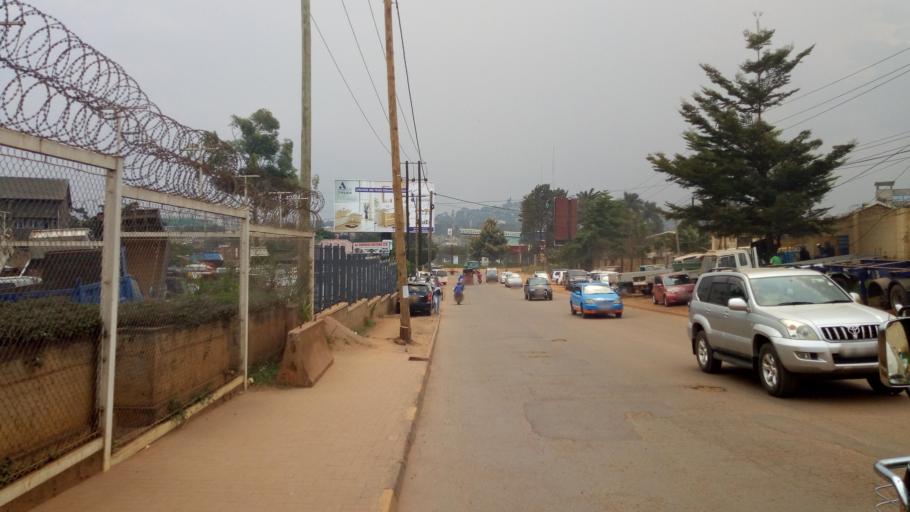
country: UG
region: Central Region
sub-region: Kampala District
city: Kampala
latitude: 0.3215
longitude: 32.6109
